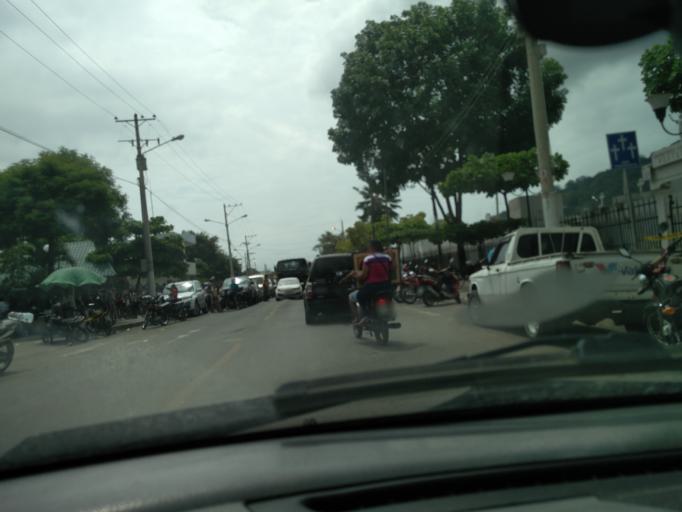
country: EC
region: Manabi
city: Portoviejo
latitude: -1.0543
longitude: -80.4478
